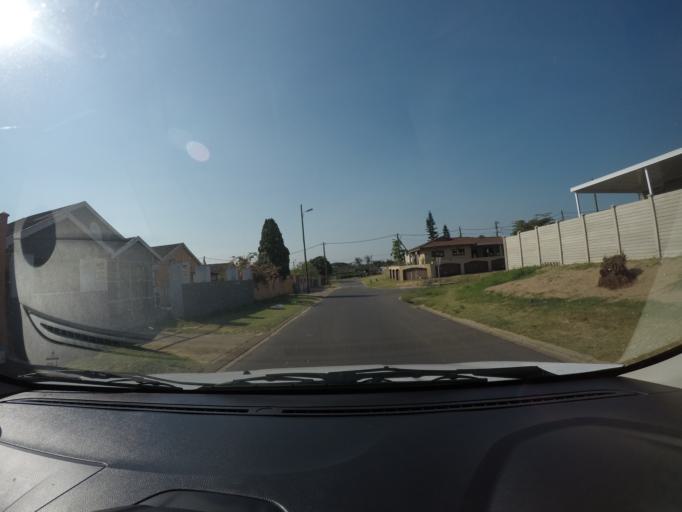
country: ZA
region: KwaZulu-Natal
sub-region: uThungulu District Municipality
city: Richards Bay
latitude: -28.7169
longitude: 32.0415
